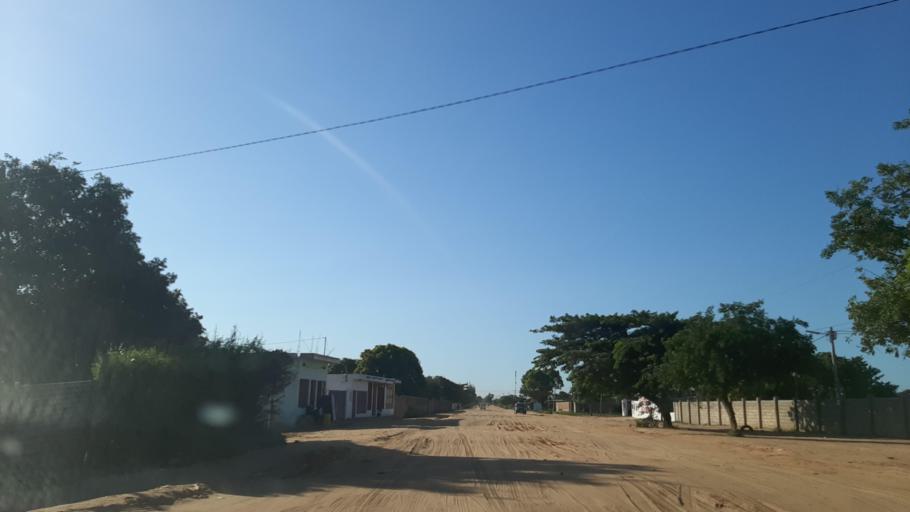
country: MZ
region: Maputo City
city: Maputo
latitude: -25.7468
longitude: 32.5447
